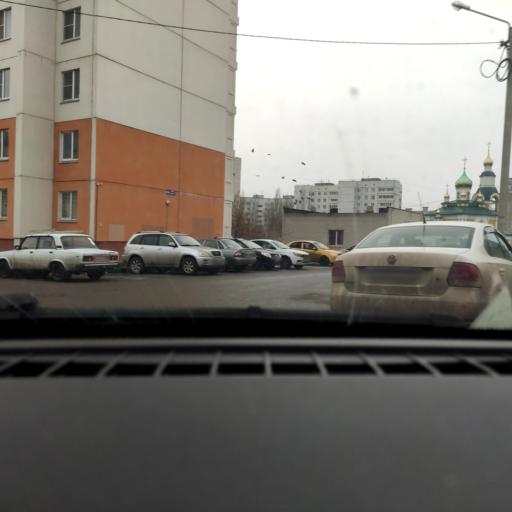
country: RU
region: Voronezj
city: Shilovo
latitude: 51.5615
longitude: 39.1158
